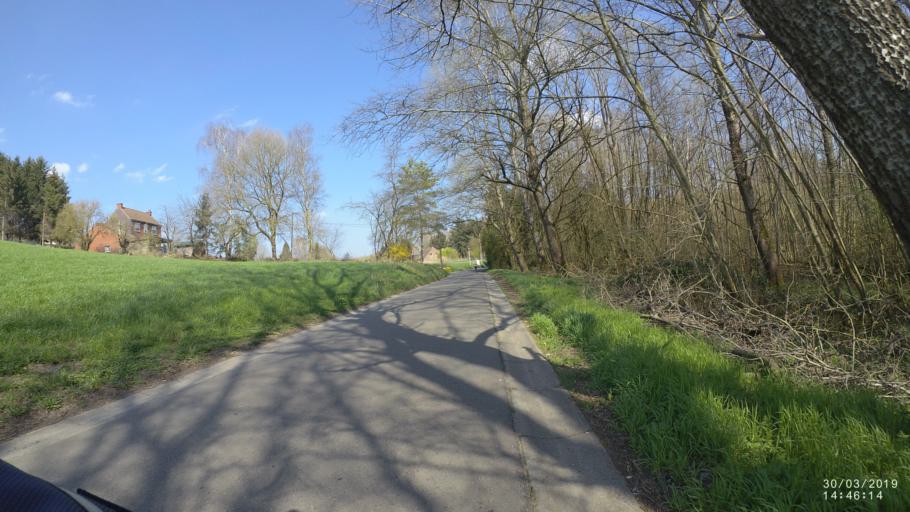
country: BE
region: Flanders
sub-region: Provincie Vlaams-Brabant
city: Overijse
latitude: 50.7496
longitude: 4.5639
